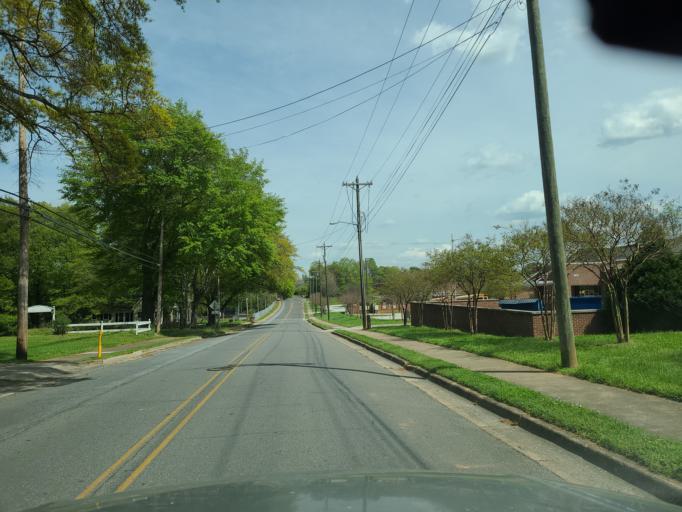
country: US
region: North Carolina
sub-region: Cleveland County
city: Shelby
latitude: 35.2936
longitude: -81.5462
